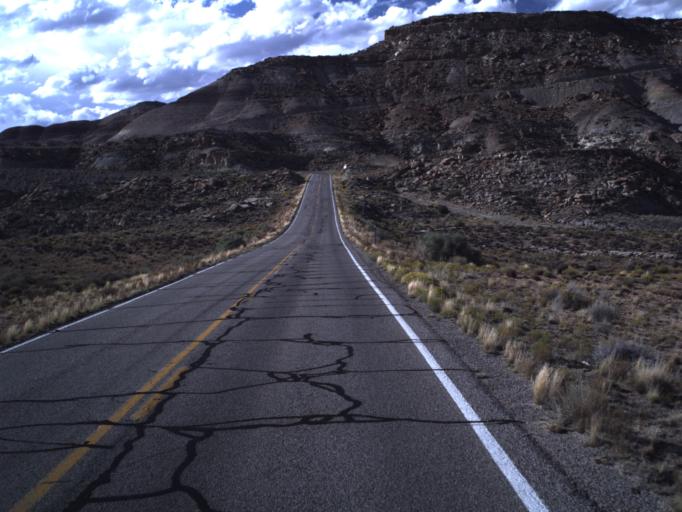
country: US
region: Utah
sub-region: San Juan County
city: Blanding
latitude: 37.3197
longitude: -109.3104
